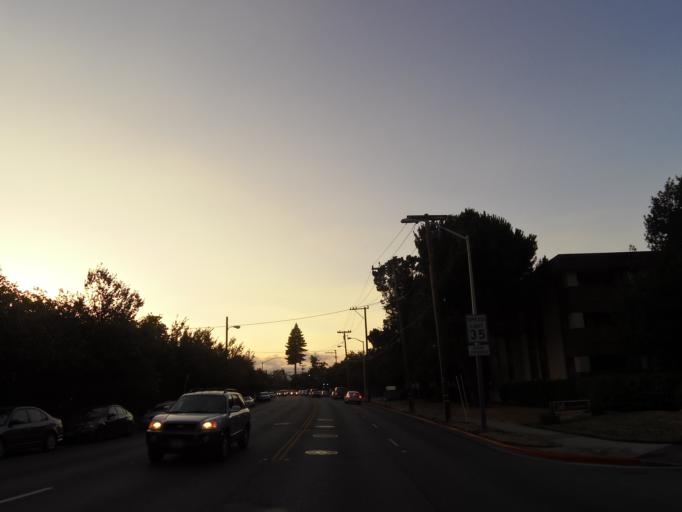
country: US
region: California
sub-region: San Mateo County
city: San Mateo
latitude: 37.5661
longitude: -122.3288
